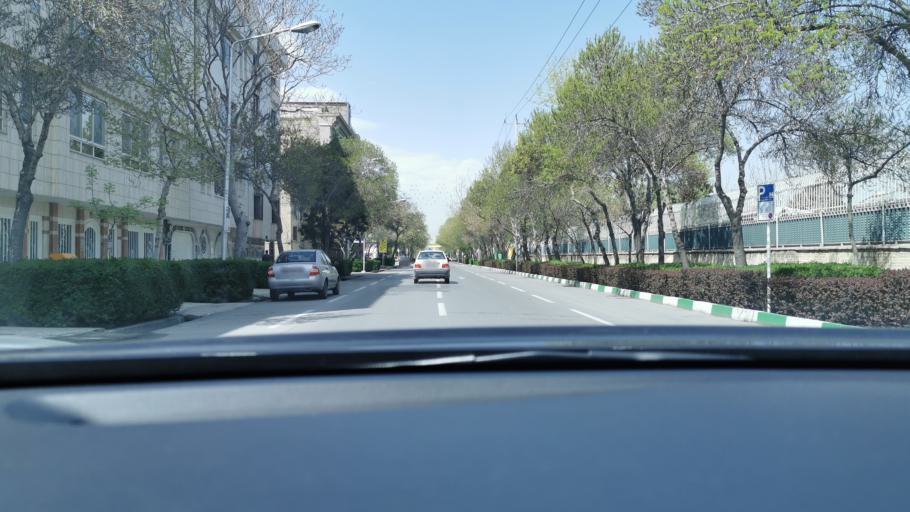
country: IR
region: Razavi Khorasan
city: Mashhad
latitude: 36.3000
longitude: 59.5873
